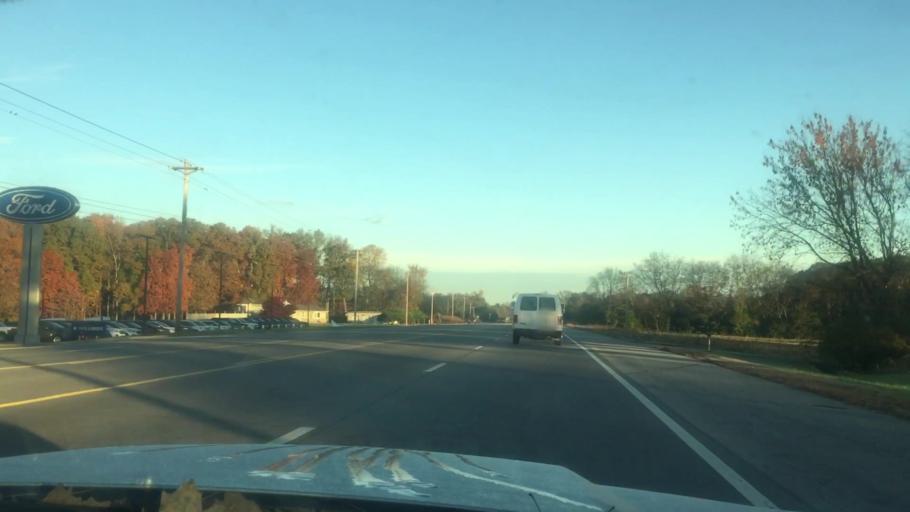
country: US
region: Tennessee
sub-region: Franklin County
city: Estill Springs
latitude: 35.2360
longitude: -86.1115
